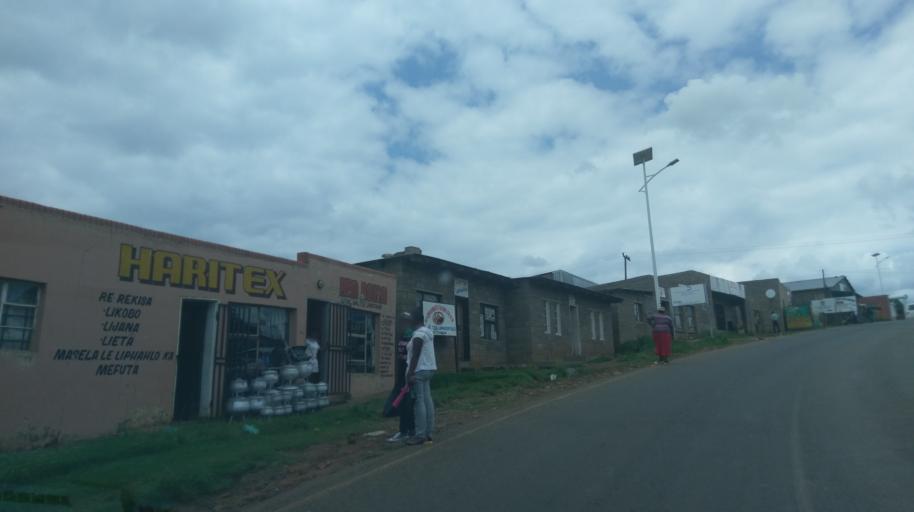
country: LS
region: Leribe
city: Leribe
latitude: -29.0001
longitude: 28.2087
